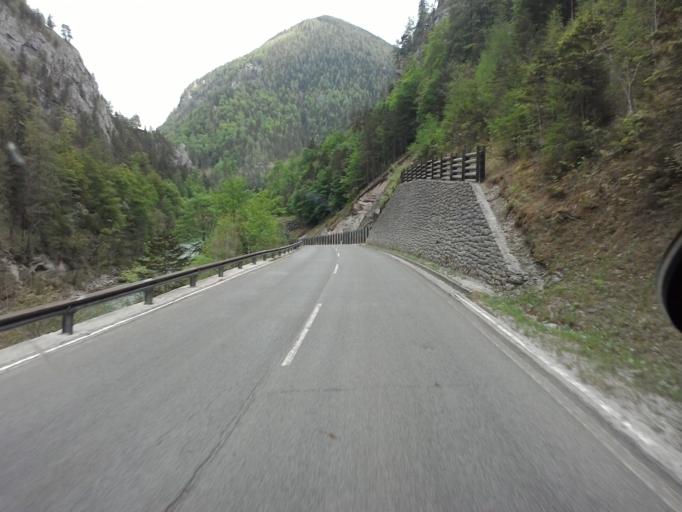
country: AT
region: Styria
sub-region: Politischer Bezirk Liezen
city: Palfau
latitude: 47.6904
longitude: 14.8778
